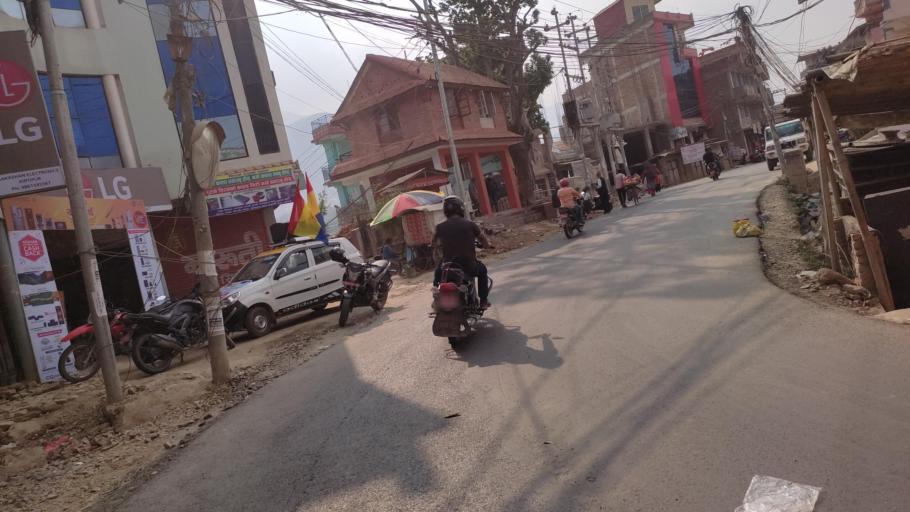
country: NP
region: Central Region
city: Kirtipur
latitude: 27.6659
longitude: 85.2653
